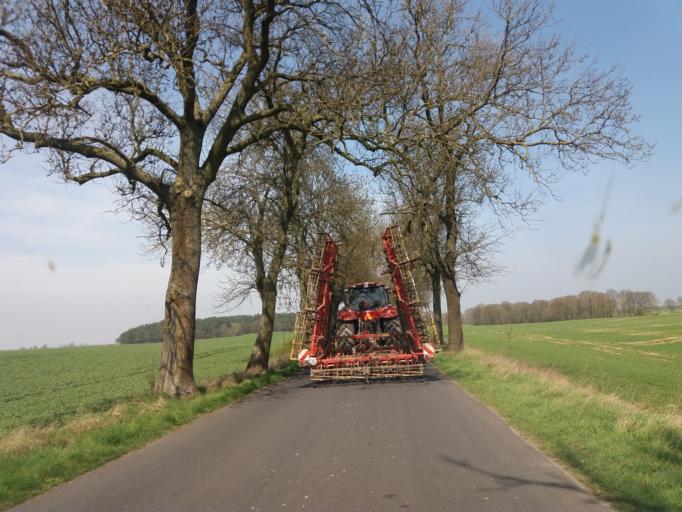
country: PL
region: West Pomeranian Voivodeship
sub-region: Powiat choszczenski
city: Recz
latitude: 53.2308
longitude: 15.6043
